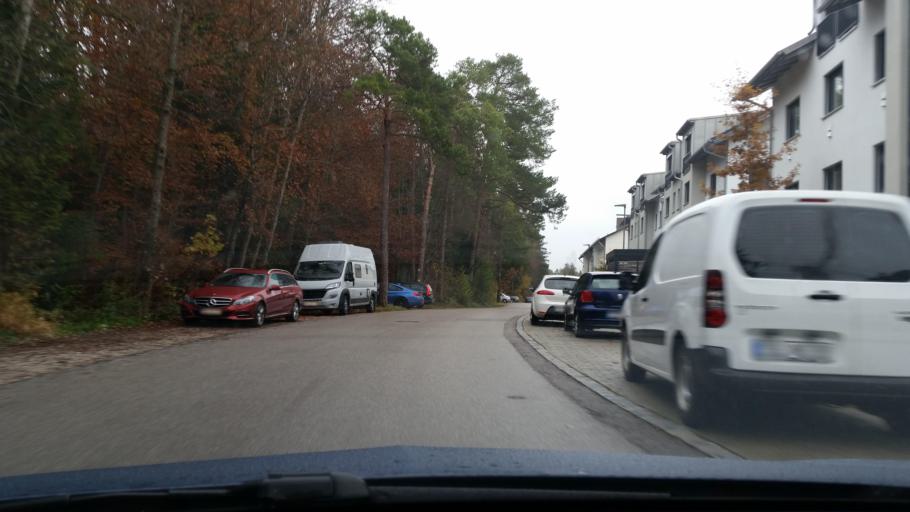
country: DE
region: Bavaria
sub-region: Upper Bavaria
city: Geretsried
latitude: 47.8889
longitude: 11.4684
